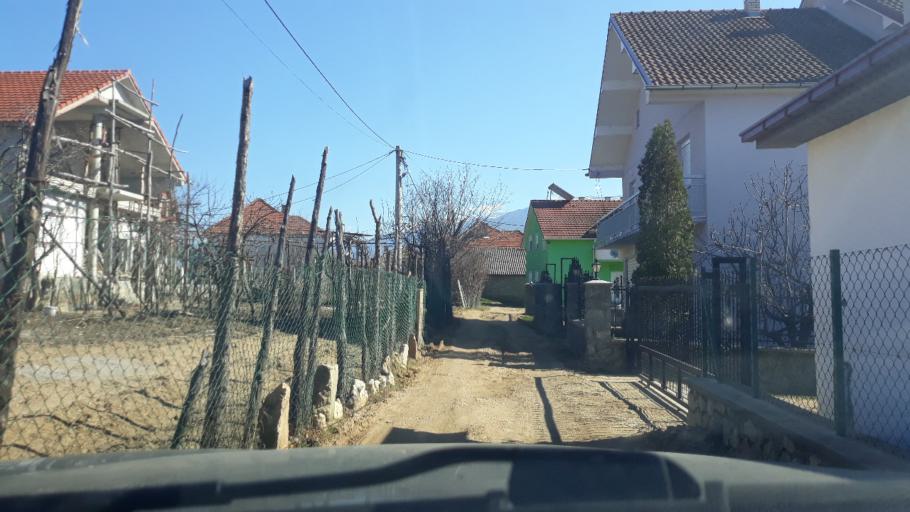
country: MK
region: Novo Selo
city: Novo Selo
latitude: 41.4177
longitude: 22.8793
